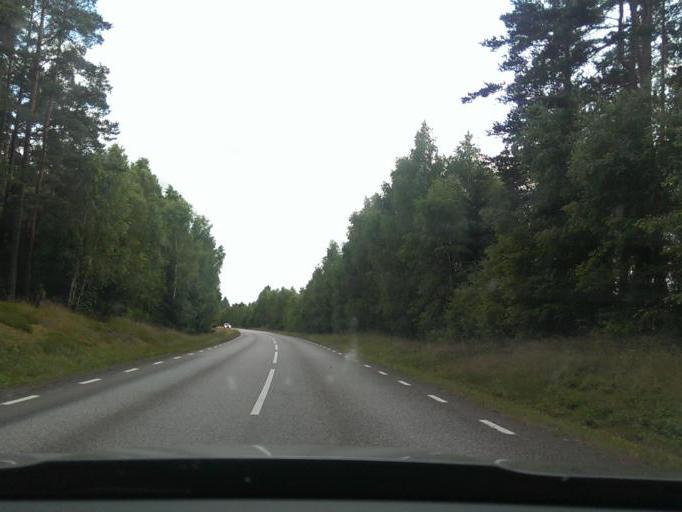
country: SE
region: Kronoberg
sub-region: Ljungby Kommun
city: Lagan
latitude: 56.9339
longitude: 13.9792
